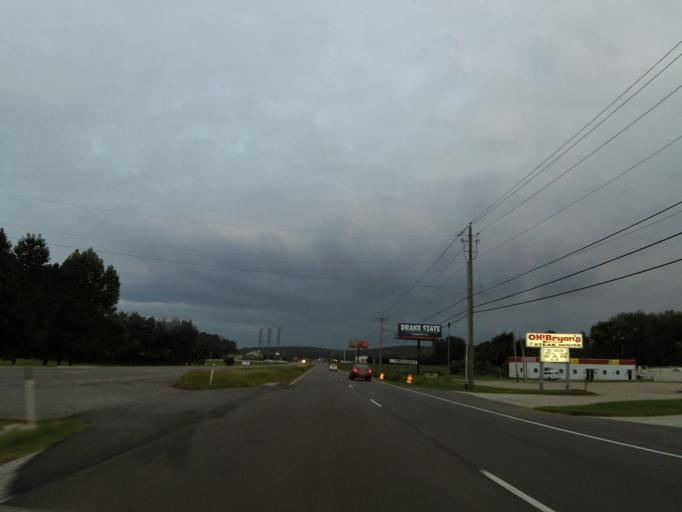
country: US
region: Alabama
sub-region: Madison County
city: Moores Mill
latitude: 34.7720
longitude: -86.5147
